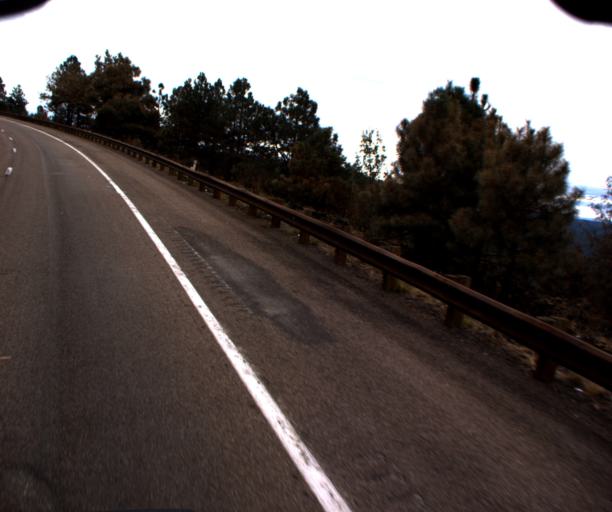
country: US
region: Arizona
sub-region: Gila County
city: Star Valley
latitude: 34.3001
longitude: -110.9071
